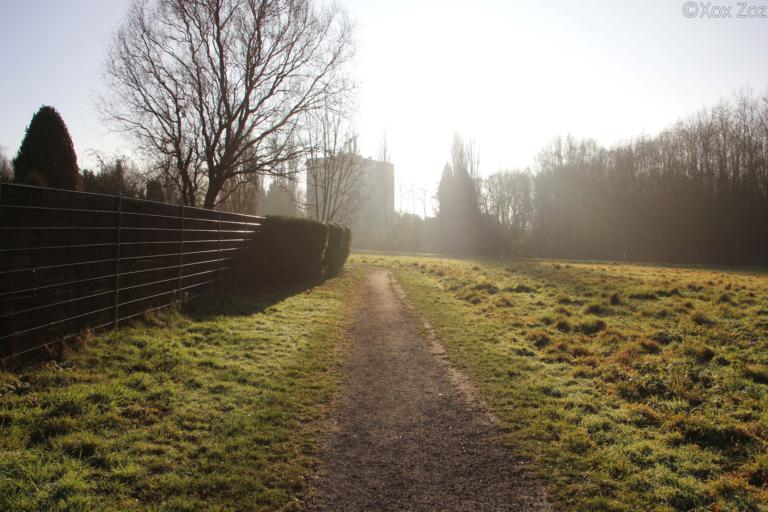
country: DE
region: North Rhine-Westphalia
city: Witten
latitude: 51.4855
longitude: 7.3226
